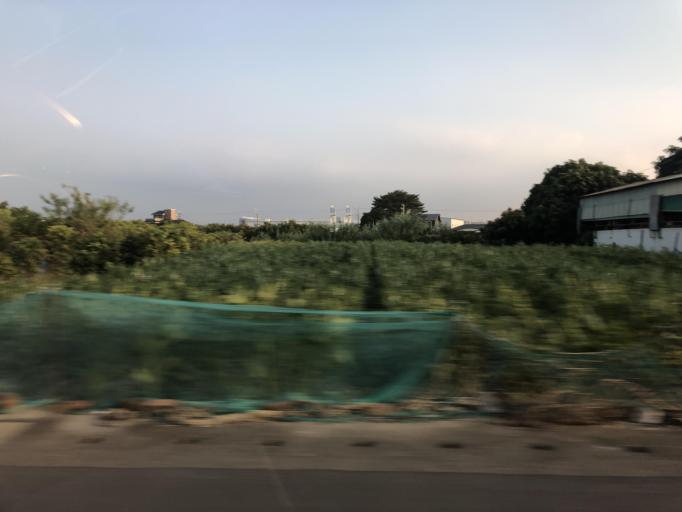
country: TW
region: Taiwan
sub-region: Tainan
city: Tainan
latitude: 23.1327
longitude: 120.2565
